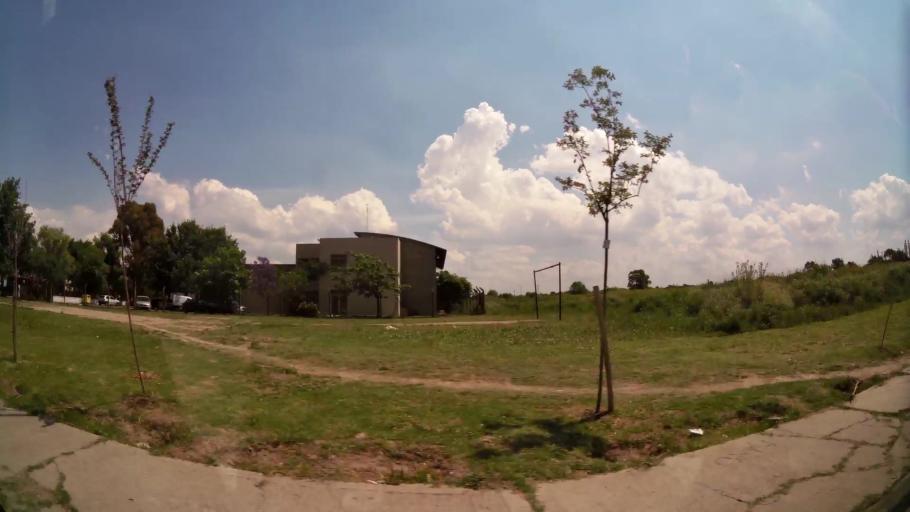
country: AR
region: Buenos Aires
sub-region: Partido de Tigre
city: Tigre
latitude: -34.4630
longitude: -58.5826
